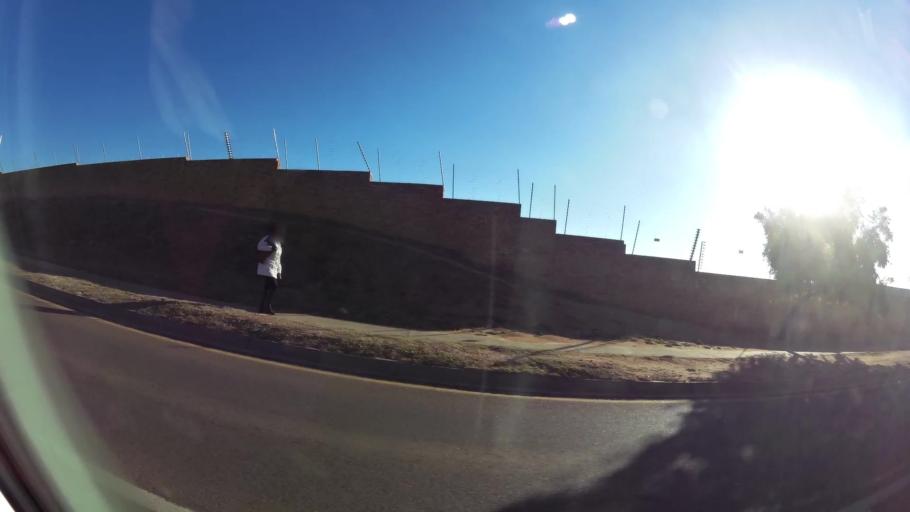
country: ZA
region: Gauteng
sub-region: City of Johannesburg Metropolitan Municipality
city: Midrand
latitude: -25.9016
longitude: 28.1051
